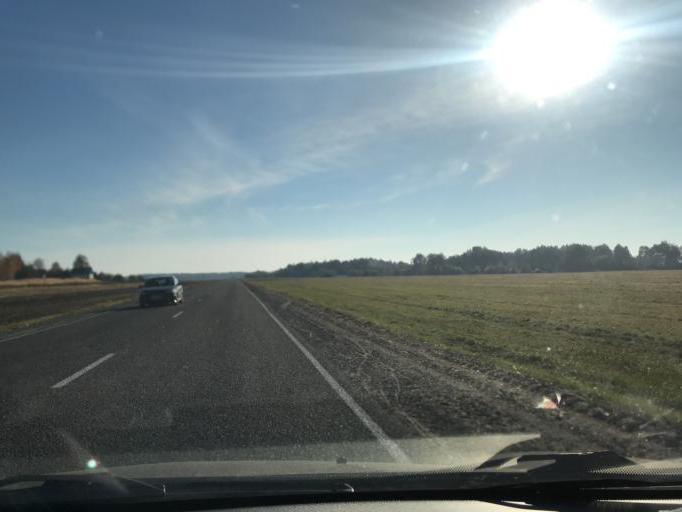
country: BY
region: Gomel
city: Brahin
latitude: 51.7740
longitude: 30.2649
